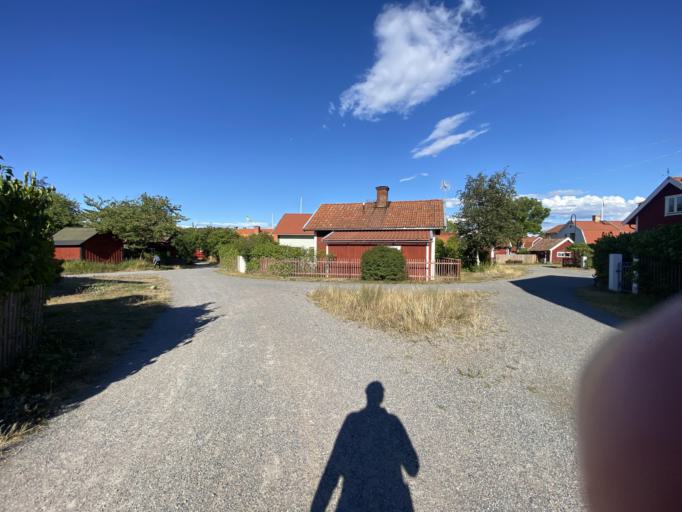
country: SE
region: Stockholm
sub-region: Varmdo Kommun
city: Holo
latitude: 59.2888
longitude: 18.9109
